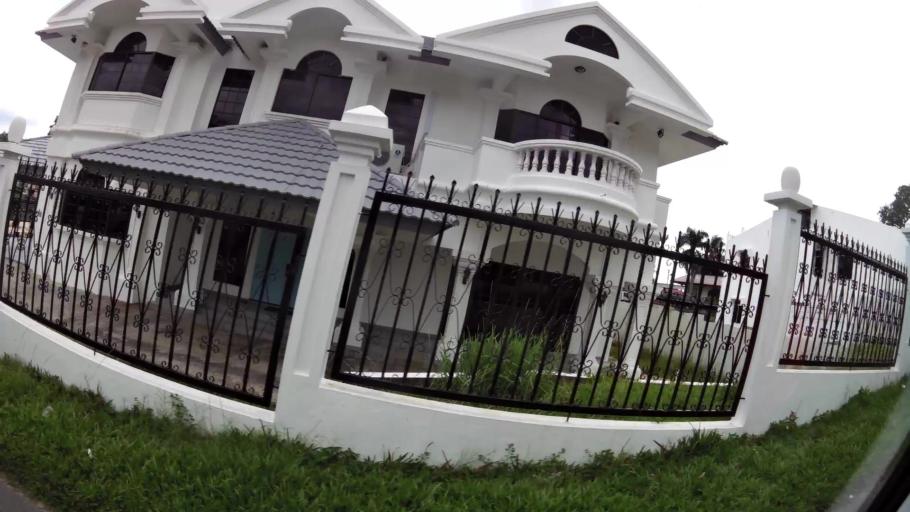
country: BN
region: Brunei and Muara
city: Bandar Seri Begawan
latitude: 4.9535
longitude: 114.9642
